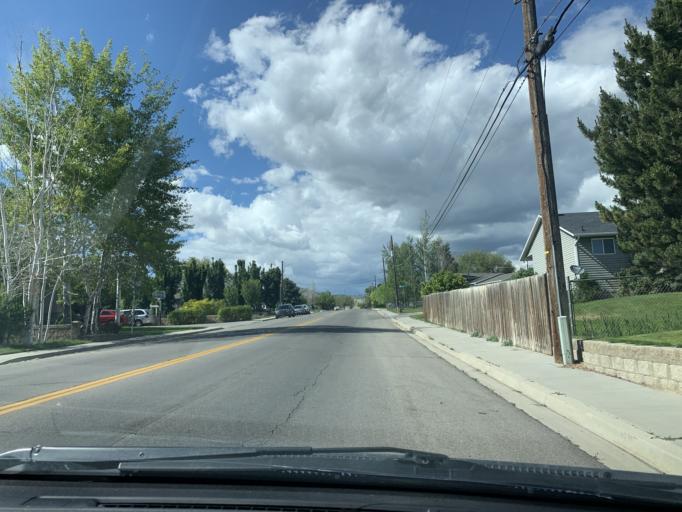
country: US
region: Utah
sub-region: Utah County
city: Lehi
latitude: 40.4017
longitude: -111.8398
